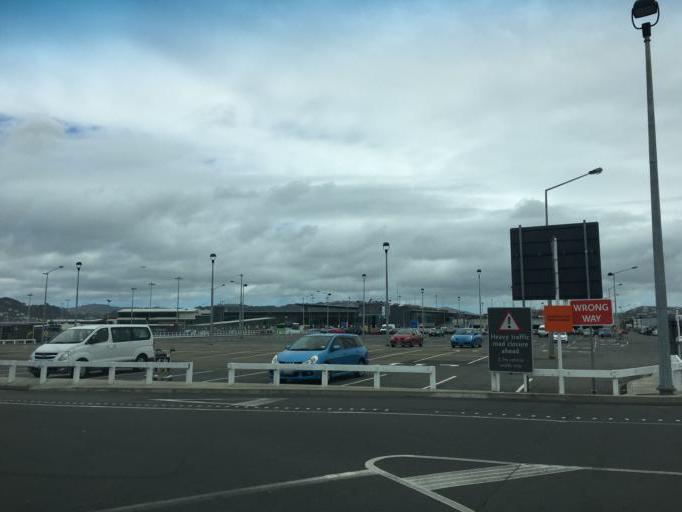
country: NZ
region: Wellington
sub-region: Wellington City
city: Wellington
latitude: -41.3324
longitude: 174.8127
